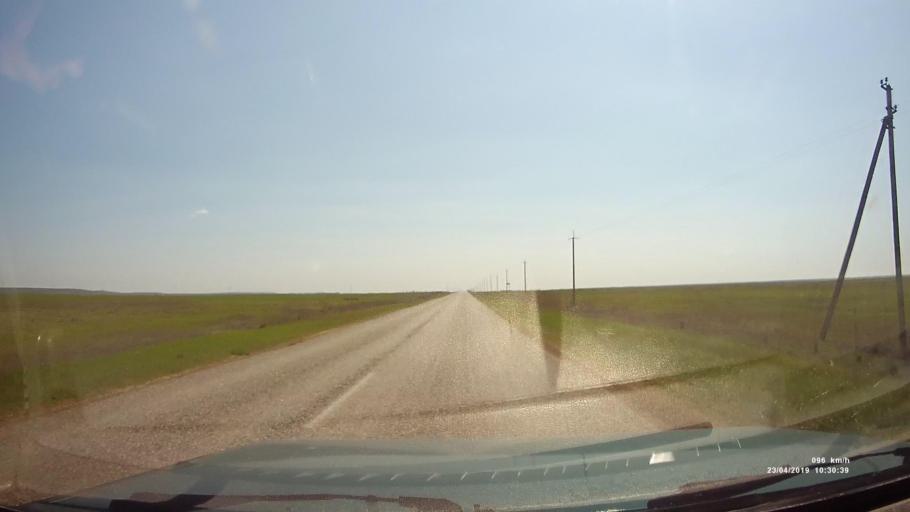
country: RU
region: Kalmykiya
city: Yashalta
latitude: 46.5908
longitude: 42.5484
